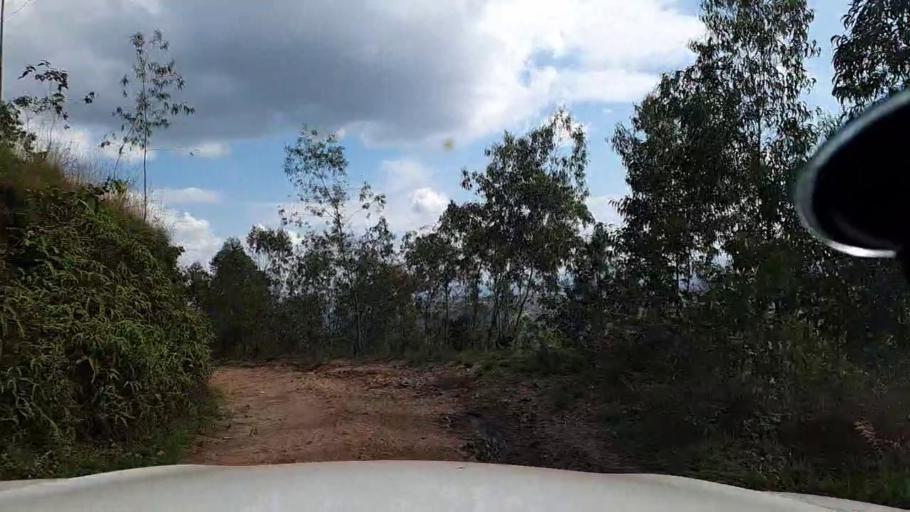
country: RW
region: Kigali
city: Kigali
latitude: -1.7863
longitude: 29.8385
